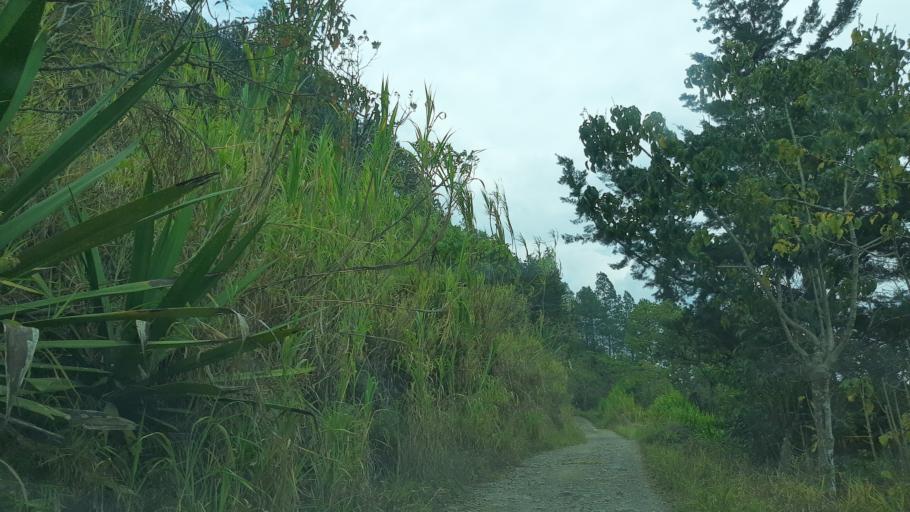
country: CO
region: Cundinamarca
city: Tenza
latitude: 5.0814
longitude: -73.4005
